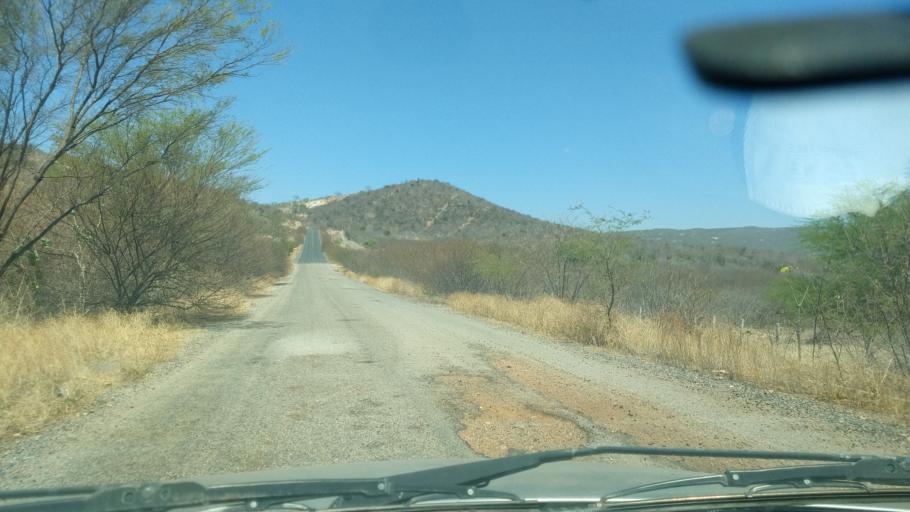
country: BR
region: Rio Grande do Norte
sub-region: Sao Tome
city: Sao Tome
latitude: -5.9714
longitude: -36.1533
